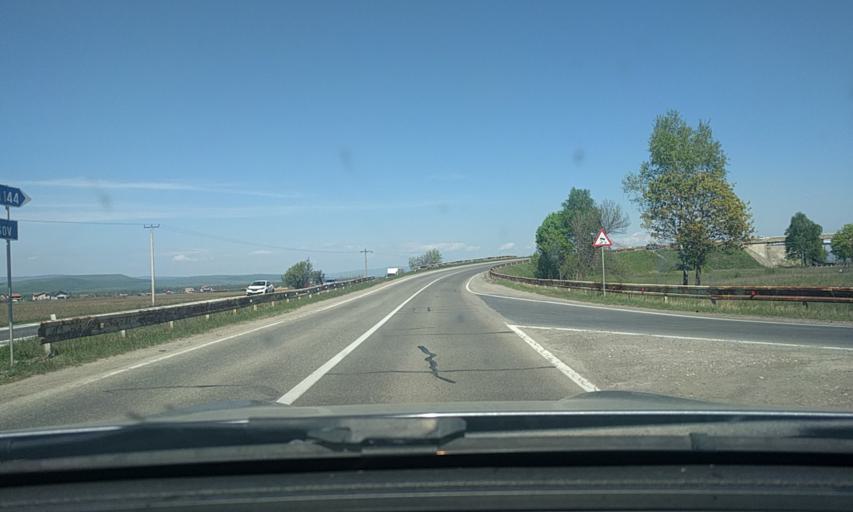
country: RO
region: Brasov
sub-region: Comuna Harman
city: Harman
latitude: 45.7099
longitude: 25.7042
